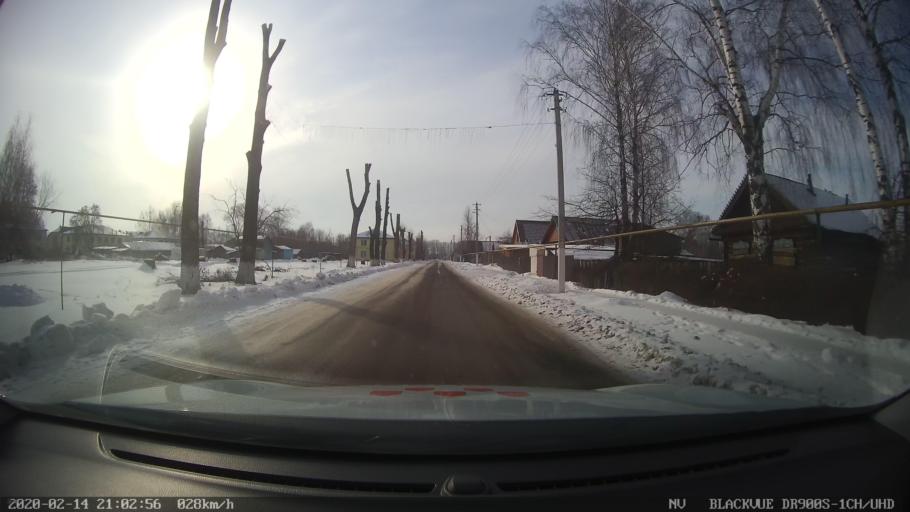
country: RU
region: Tatarstan
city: Kuybyshevskiy Zaton
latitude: 55.1586
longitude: 49.1773
